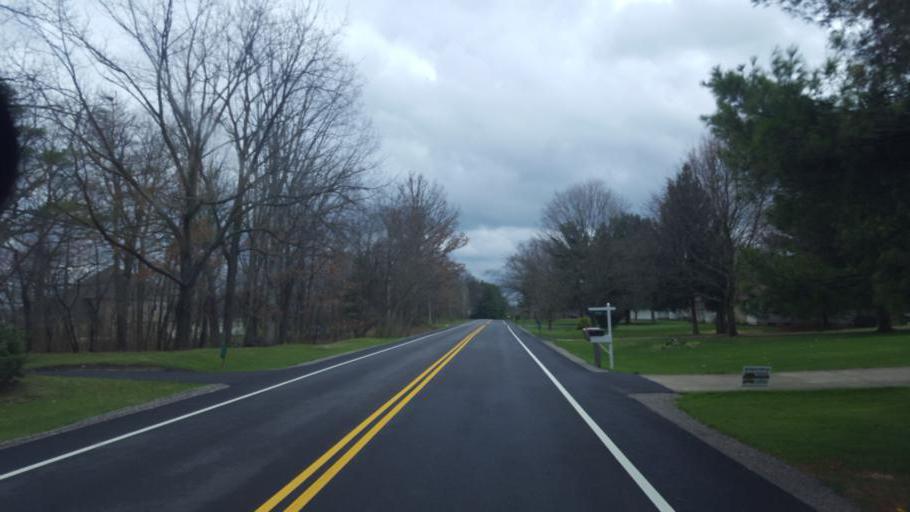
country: US
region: Ohio
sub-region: Delaware County
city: Sunbury
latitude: 40.2027
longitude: -82.8953
